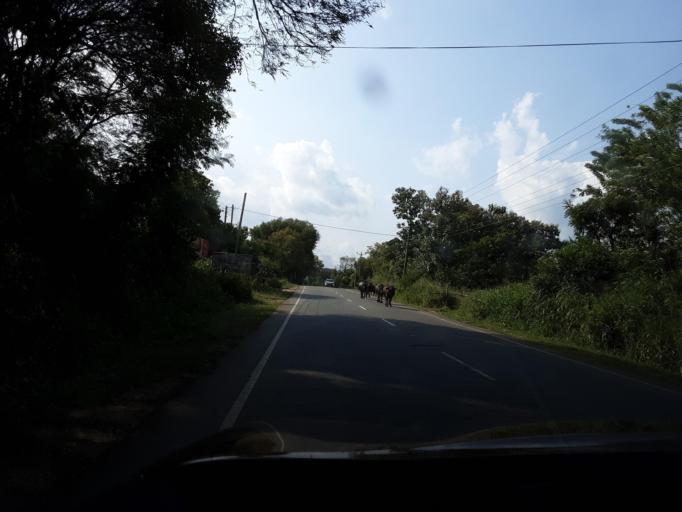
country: LK
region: Uva
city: Haputale
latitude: 6.6076
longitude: 81.1352
